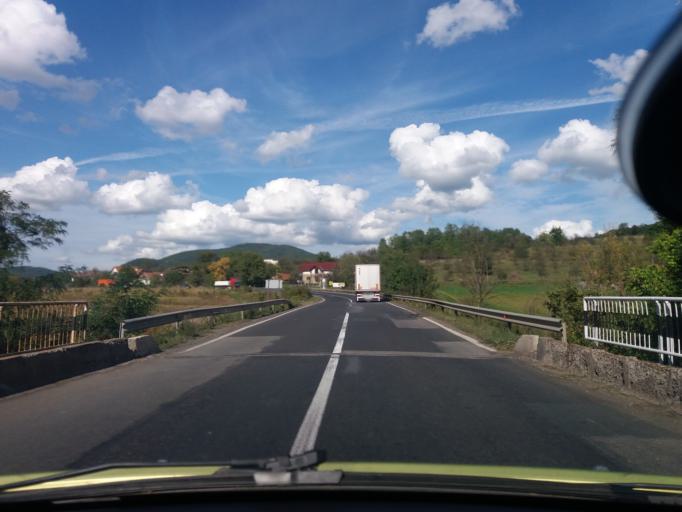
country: RO
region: Hunedoara
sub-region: Comuna Zam
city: Zam
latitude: 45.9880
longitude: 22.4349
